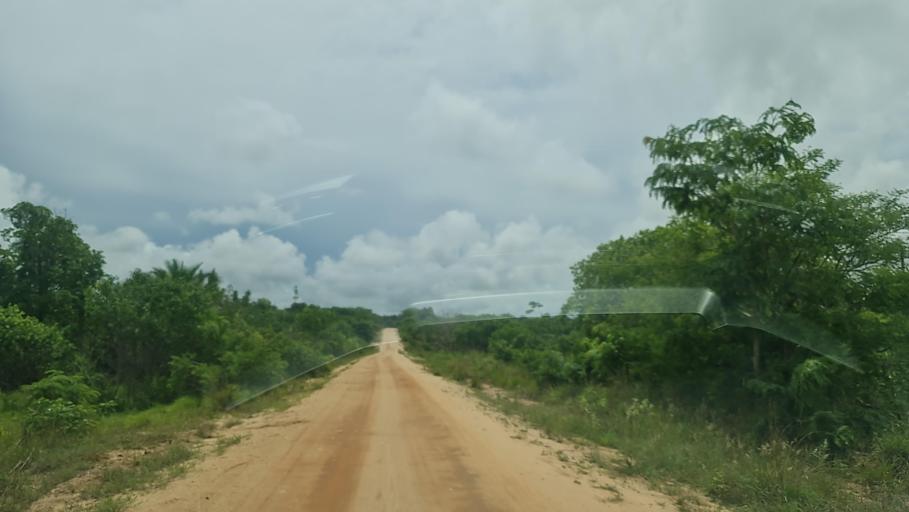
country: MZ
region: Zambezia
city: Quelimane
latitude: -17.2686
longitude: 37.2520
